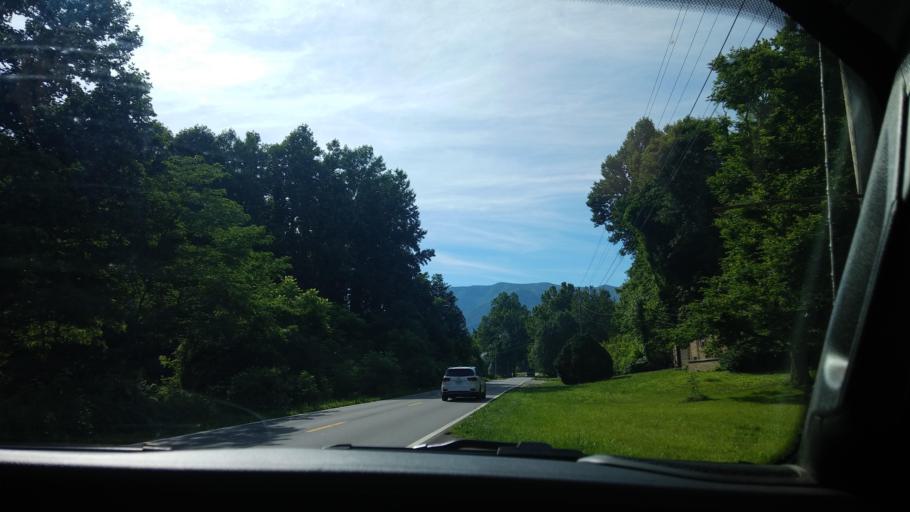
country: US
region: Tennessee
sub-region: Cocke County
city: Newport
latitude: 35.7861
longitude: -83.2263
